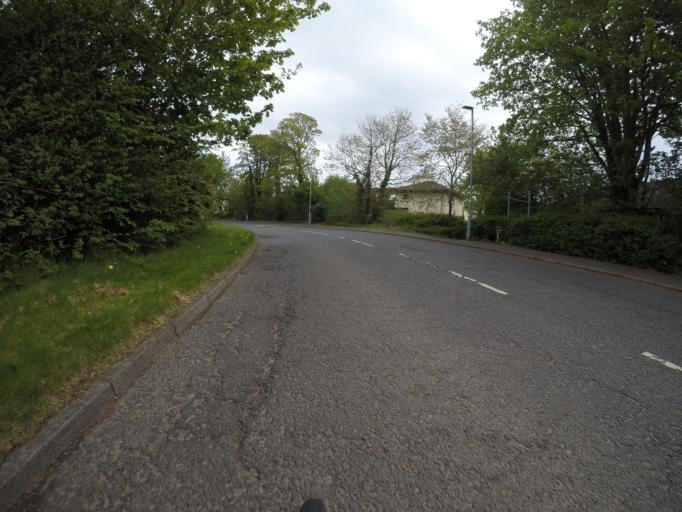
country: GB
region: Scotland
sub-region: North Ayrshire
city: Irvine
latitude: 55.6277
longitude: -4.6335
